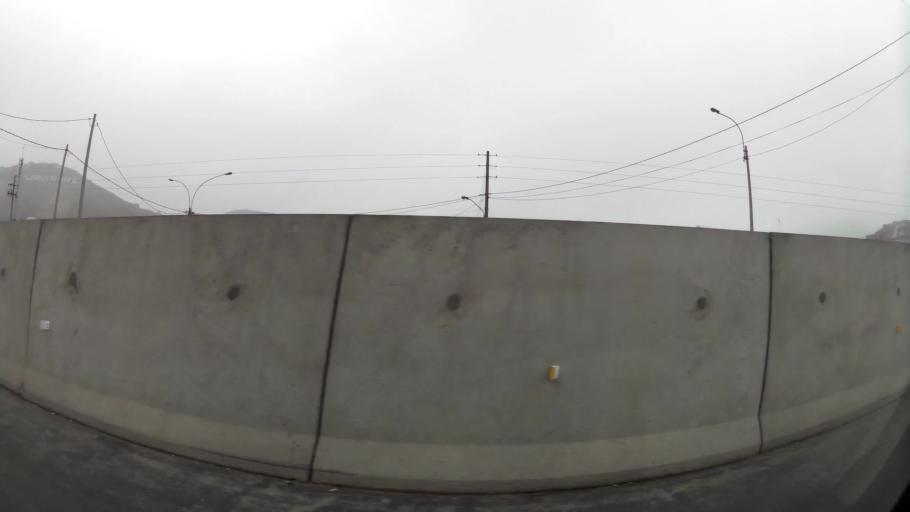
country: PE
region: Lima
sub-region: Lima
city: Santa Rosa
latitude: -11.8139
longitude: -77.1289
